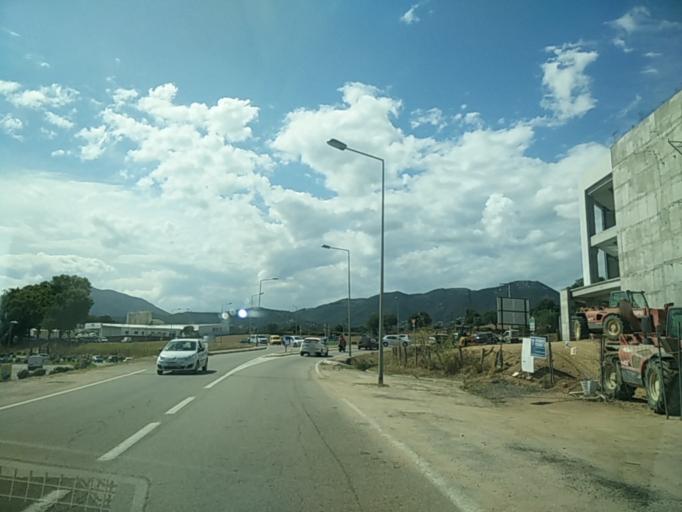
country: FR
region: Corsica
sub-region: Departement de la Corse-du-Sud
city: Afa
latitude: 41.9549
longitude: 8.7970
